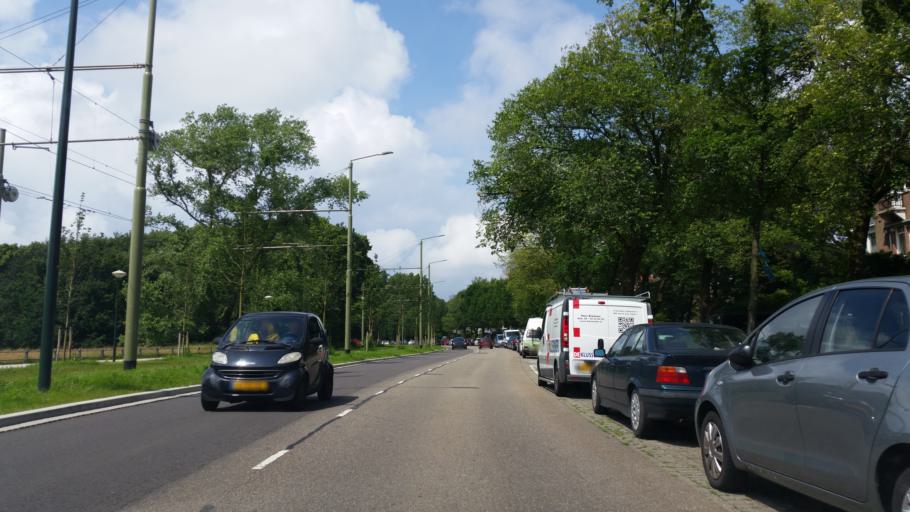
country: NL
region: South Holland
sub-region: Gemeente Den Haag
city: Scheveningen
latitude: 52.1029
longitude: 4.2961
